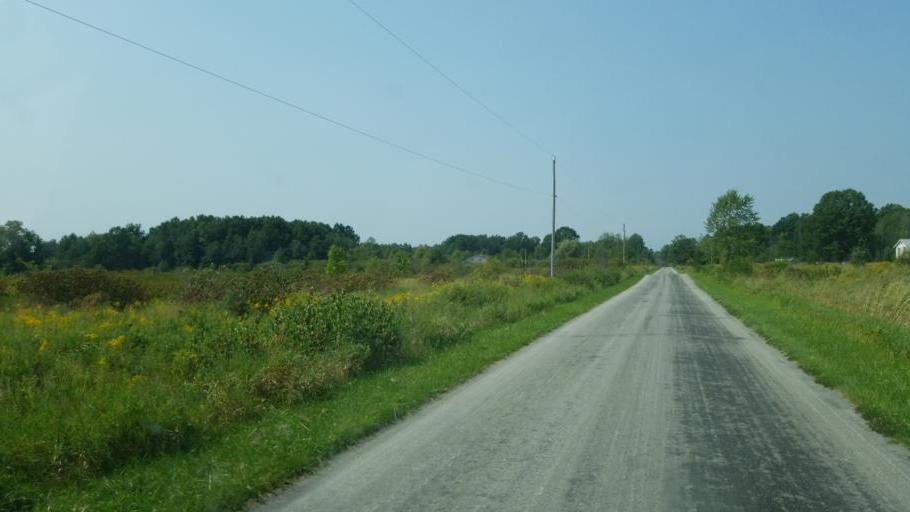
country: US
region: Ohio
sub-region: Ashtabula County
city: Orwell
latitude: 41.4891
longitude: -80.8898
